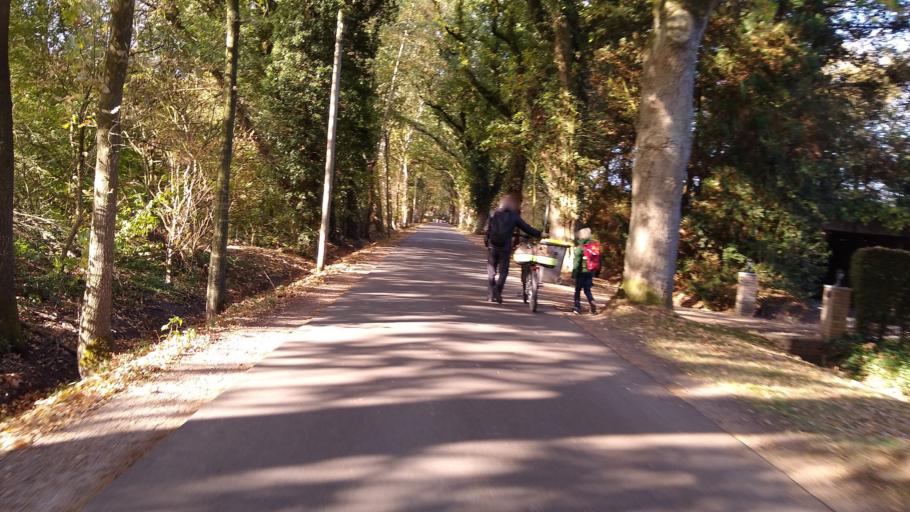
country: DE
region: Lower Saxony
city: Oldenburg
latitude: 53.1889
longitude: 8.2381
